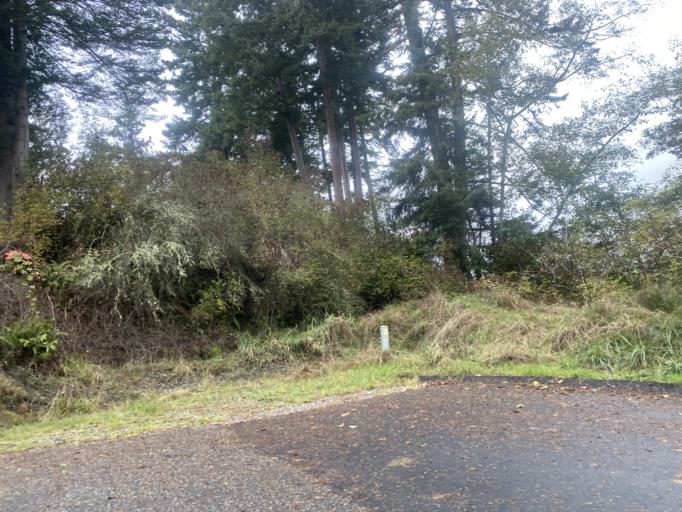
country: US
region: Washington
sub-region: Island County
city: Camano
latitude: 48.0948
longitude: -122.4953
